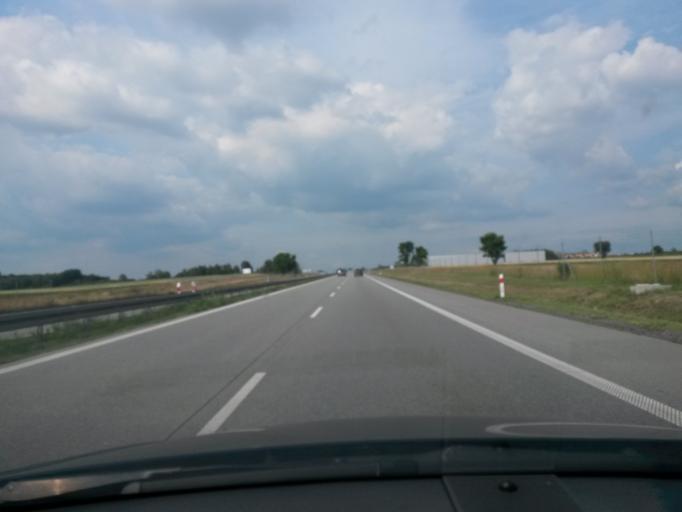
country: PL
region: Lodz Voivodeship
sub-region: Powiat rawski
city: Rawa Mazowiecka
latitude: 51.7926
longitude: 20.2892
